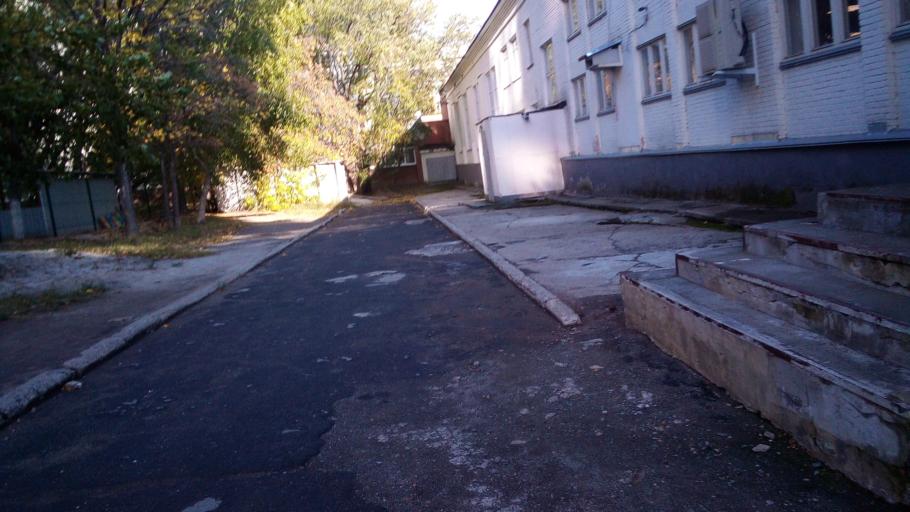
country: RU
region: Chelyabinsk
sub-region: Gorod Chelyabinsk
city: Chelyabinsk
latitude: 55.1574
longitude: 61.3661
